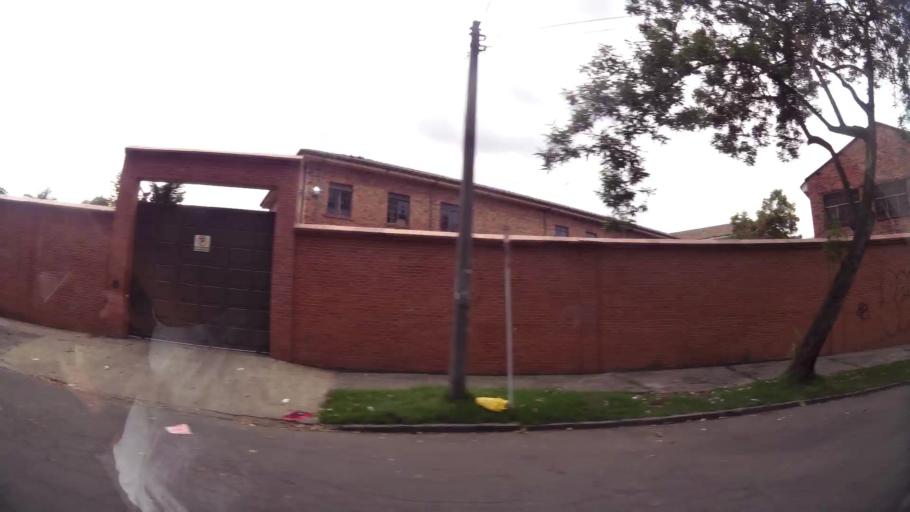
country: CO
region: Bogota D.C.
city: Bogota
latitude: 4.6509
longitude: -74.0759
